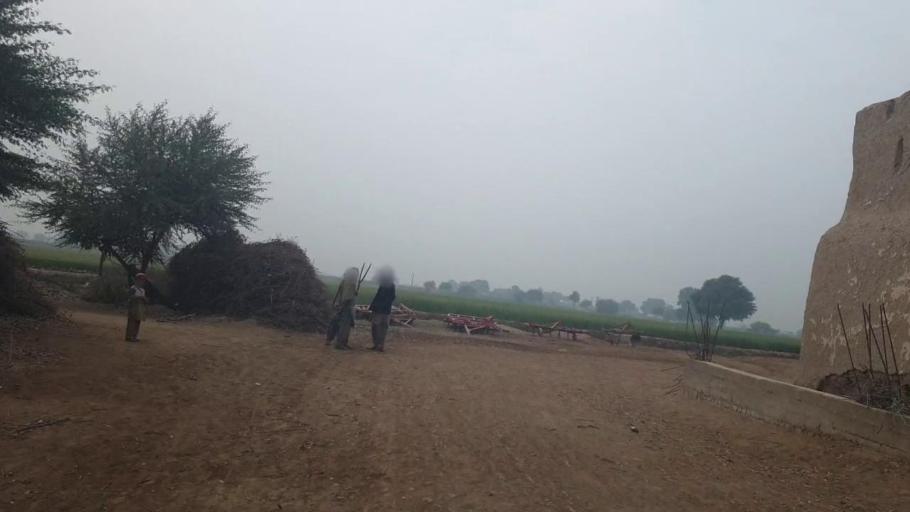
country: PK
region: Sindh
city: Tando Adam
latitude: 25.6927
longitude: 68.6574
